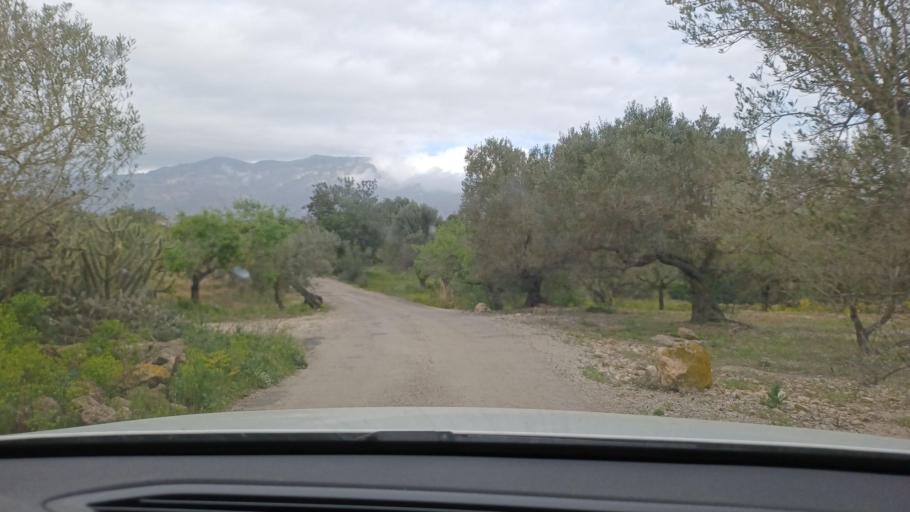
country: ES
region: Catalonia
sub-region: Provincia de Tarragona
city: Tortosa
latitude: 40.7915
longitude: 0.4745
